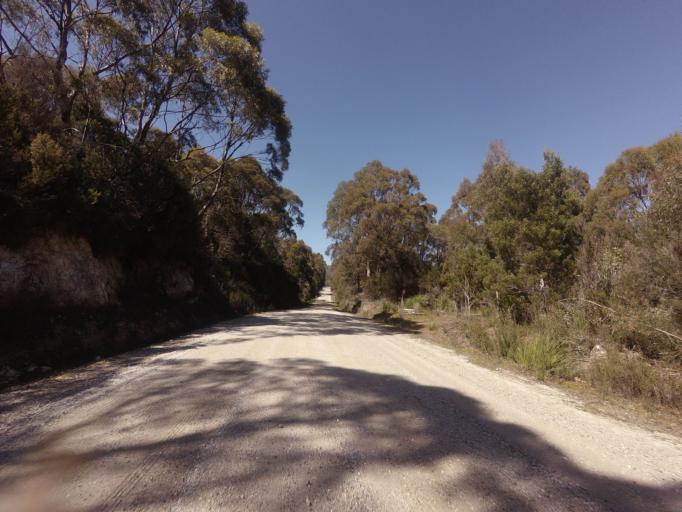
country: AU
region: Tasmania
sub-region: Huon Valley
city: Geeveston
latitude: -43.0102
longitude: 146.3635
